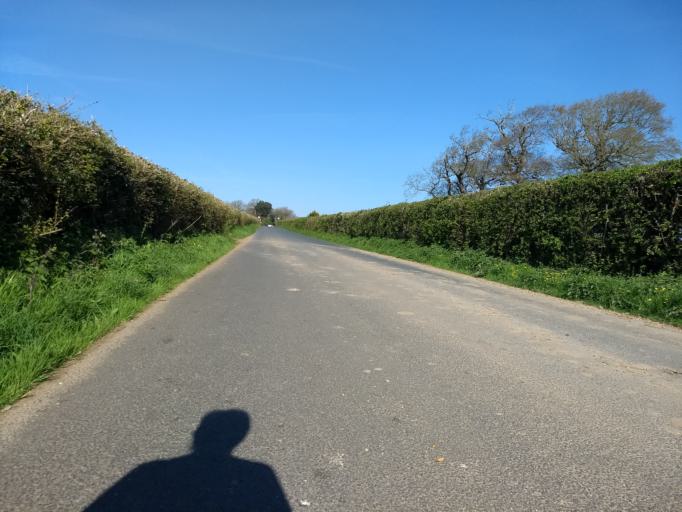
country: GB
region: England
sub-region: Isle of Wight
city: East Cowes
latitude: 50.7347
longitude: -1.2591
